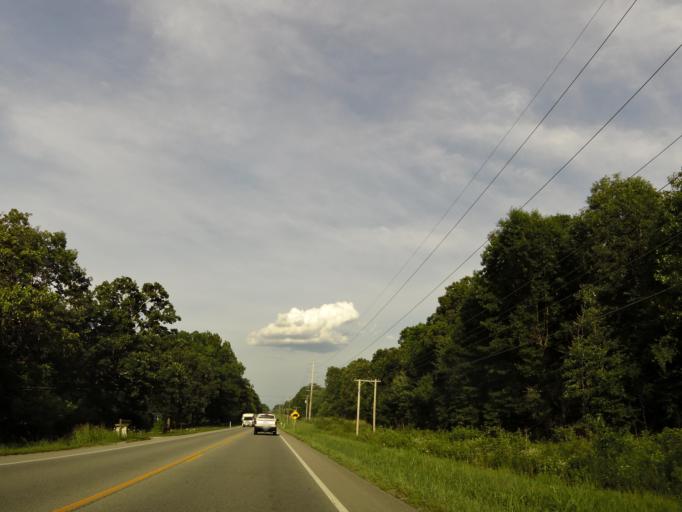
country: US
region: Tennessee
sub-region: Dickson County
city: Dickson
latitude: 36.0899
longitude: -87.4870
